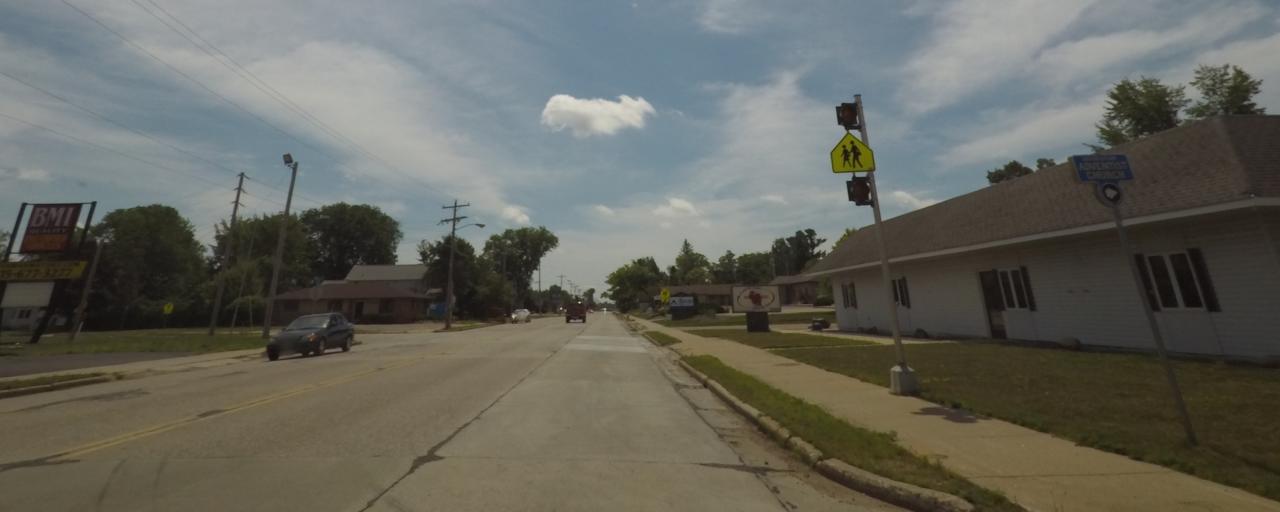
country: US
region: Wisconsin
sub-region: Portage County
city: Stevens Point
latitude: 44.5086
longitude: -89.5699
